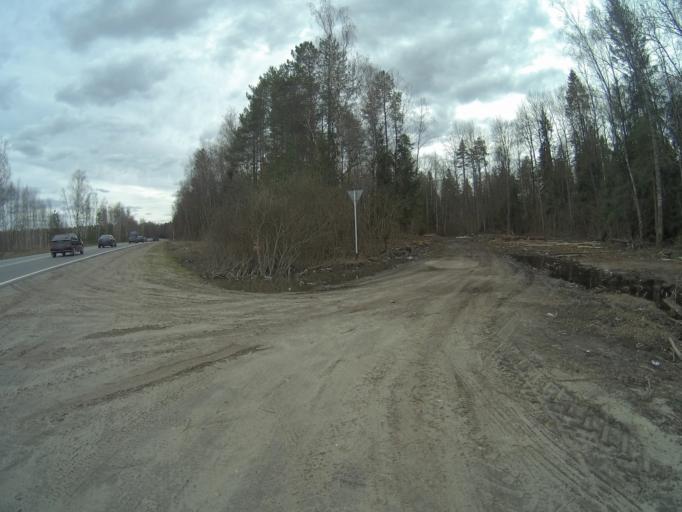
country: RU
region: Vladimir
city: Kommunar
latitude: 56.0305
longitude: 40.5622
